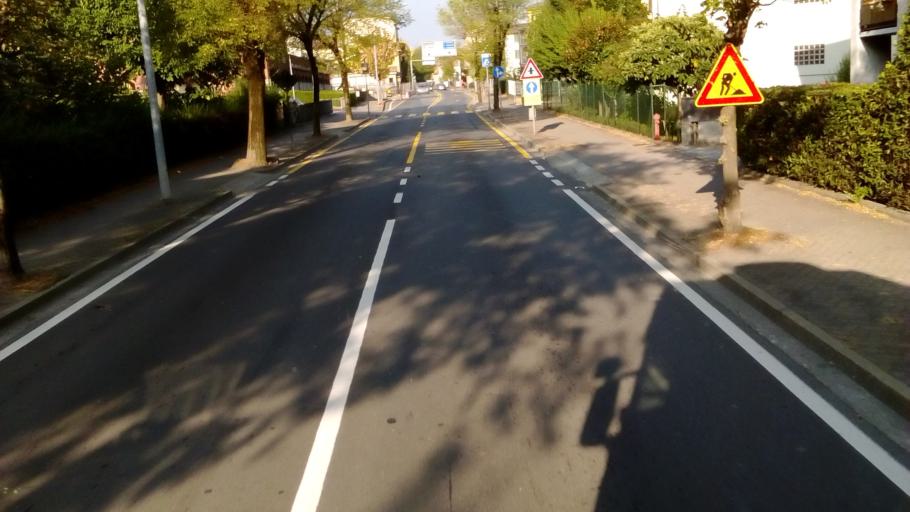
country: IT
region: Lombardy
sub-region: Provincia di Sondrio
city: Morbegno
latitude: 46.1347
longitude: 9.5765
